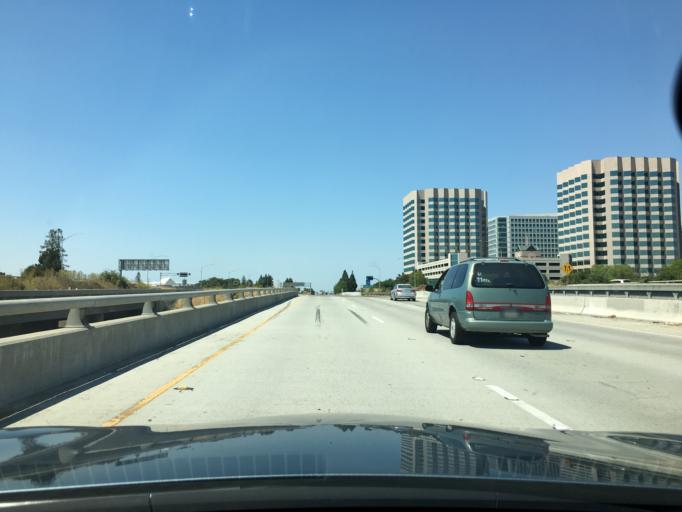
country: US
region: California
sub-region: Santa Clara County
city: San Jose
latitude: 37.3259
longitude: -121.8934
